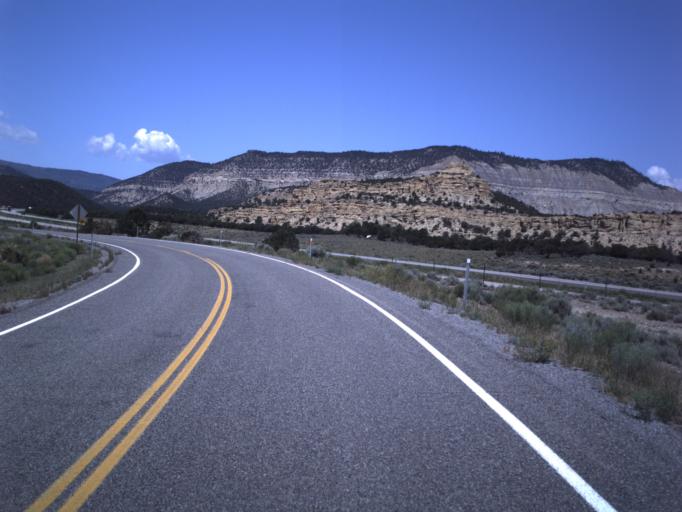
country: US
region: Utah
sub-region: Emery County
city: Ferron
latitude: 38.7556
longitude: -111.3815
